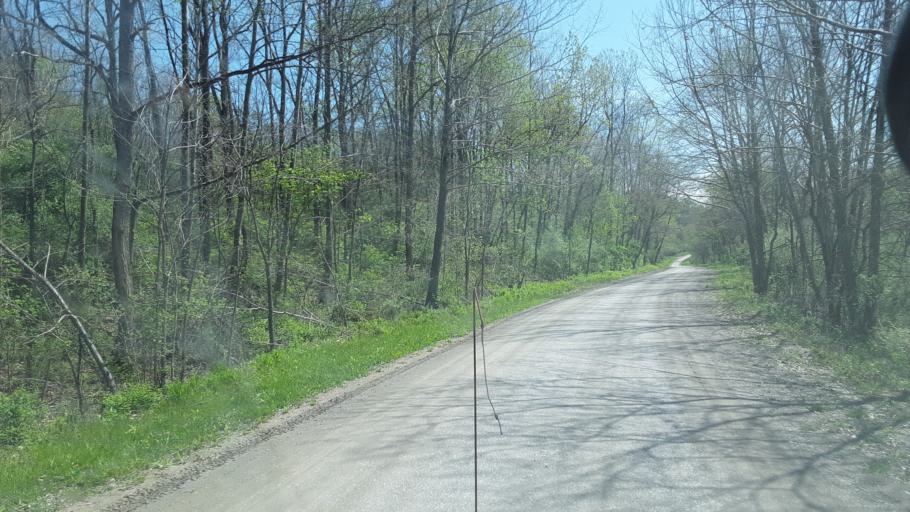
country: US
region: Ohio
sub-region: Noble County
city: Caldwell
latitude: 39.7732
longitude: -81.6282
